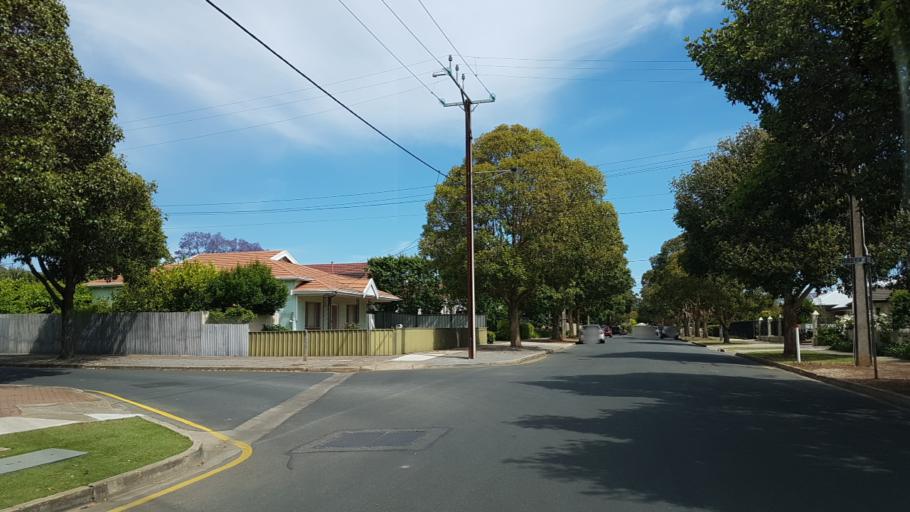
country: AU
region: South Australia
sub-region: Norwood Payneham St Peters
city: Trinity Gardens
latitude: -34.9119
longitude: 138.6485
